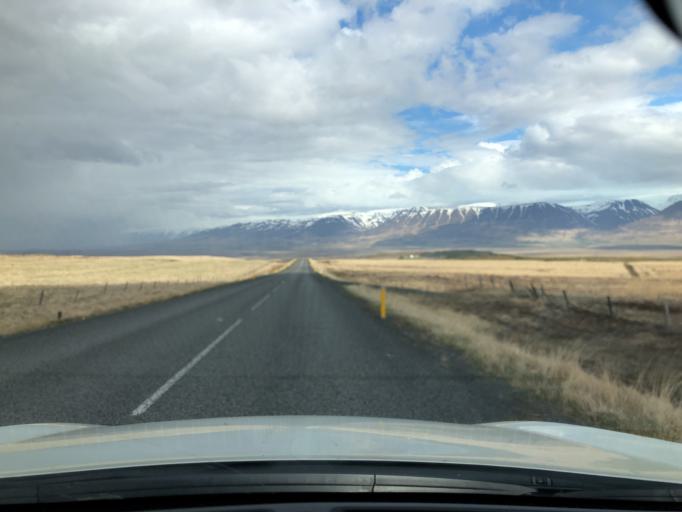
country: IS
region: Northwest
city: Saudarkrokur
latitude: 65.5371
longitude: -19.5083
